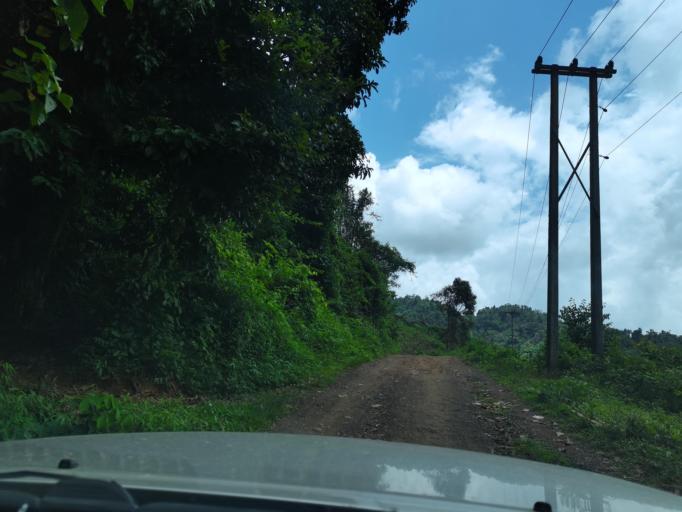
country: LA
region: Loungnamtha
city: Muang Long
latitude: 20.7468
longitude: 101.0188
